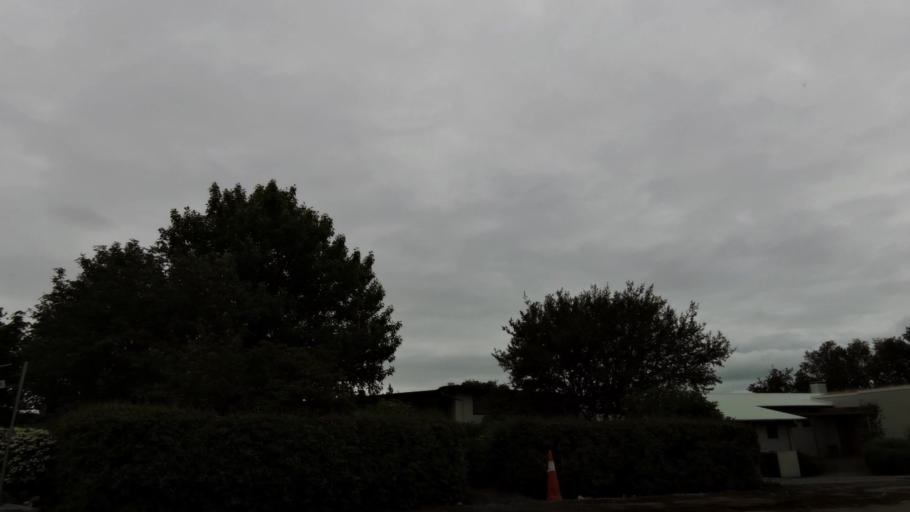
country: IS
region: Capital Region
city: Gardabaer
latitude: 64.0856
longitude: -21.9237
